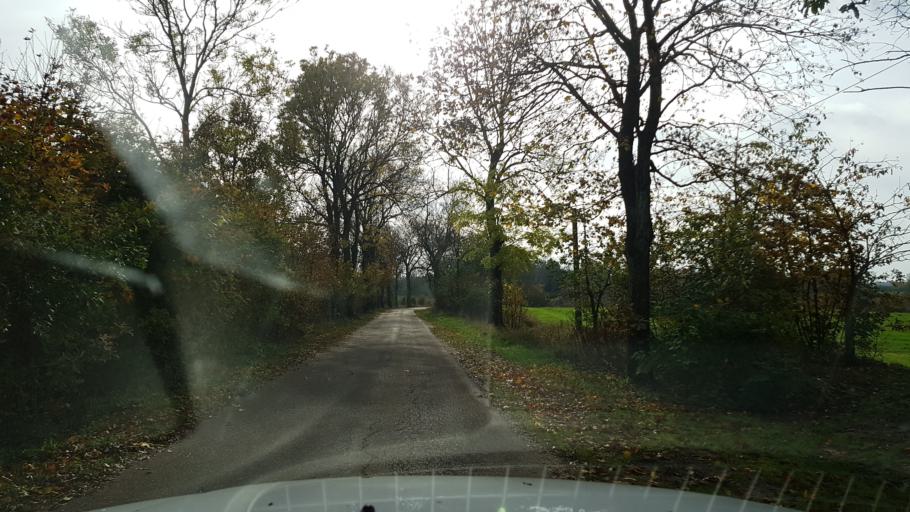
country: PL
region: West Pomeranian Voivodeship
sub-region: Powiat swidwinski
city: Polczyn-Zdroj
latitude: 53.7417
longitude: 16.0351
